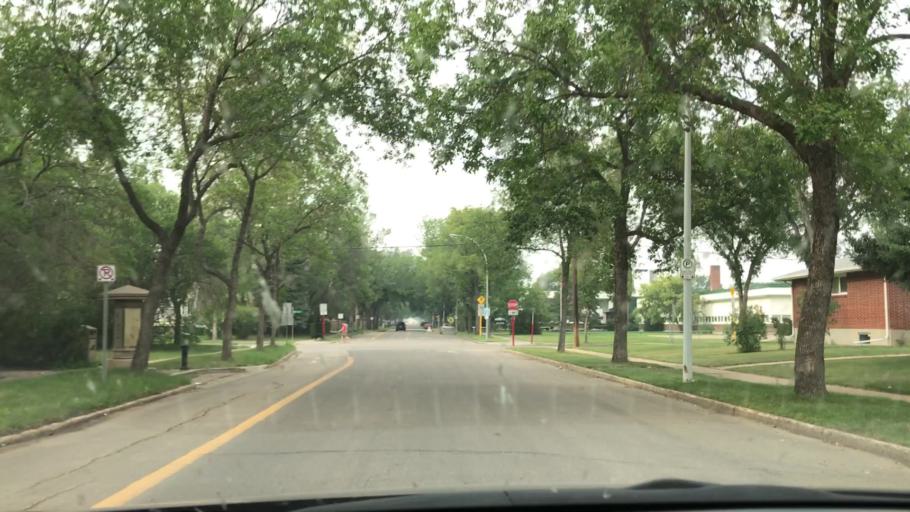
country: CA
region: Alberta
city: Edmonton
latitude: 53.5647
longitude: -113.5412
